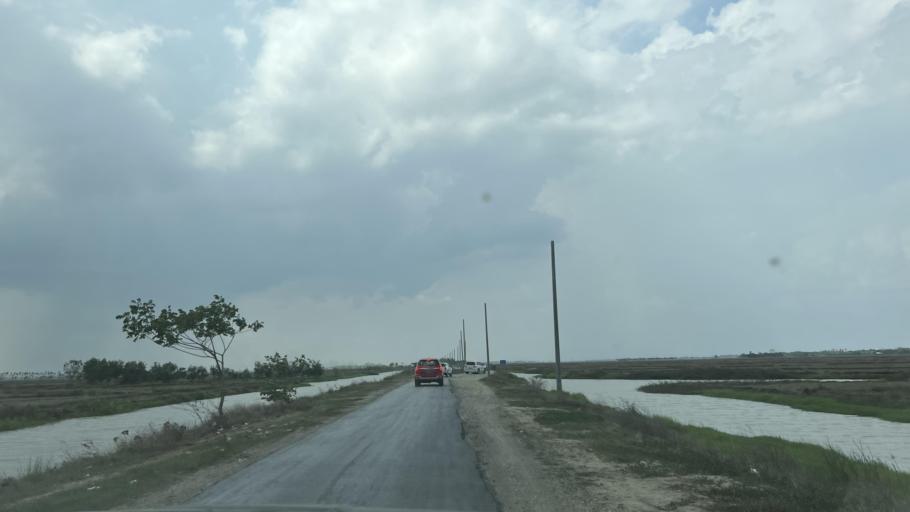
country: MM
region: Ayeyarwady
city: Pyapon
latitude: 16.0674
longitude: 95.6183
